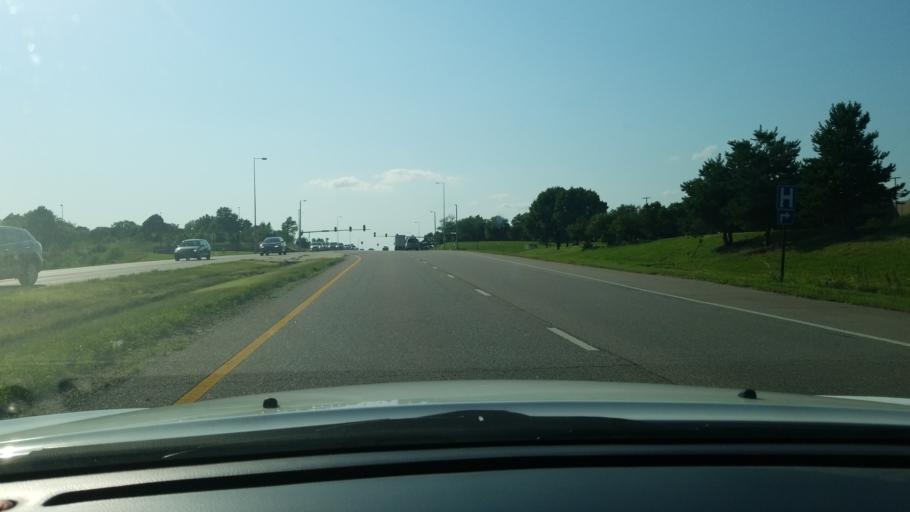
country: US
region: Nebraska
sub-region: Lancaster County
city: Lincoln
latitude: 40.7448
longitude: -96.6228
